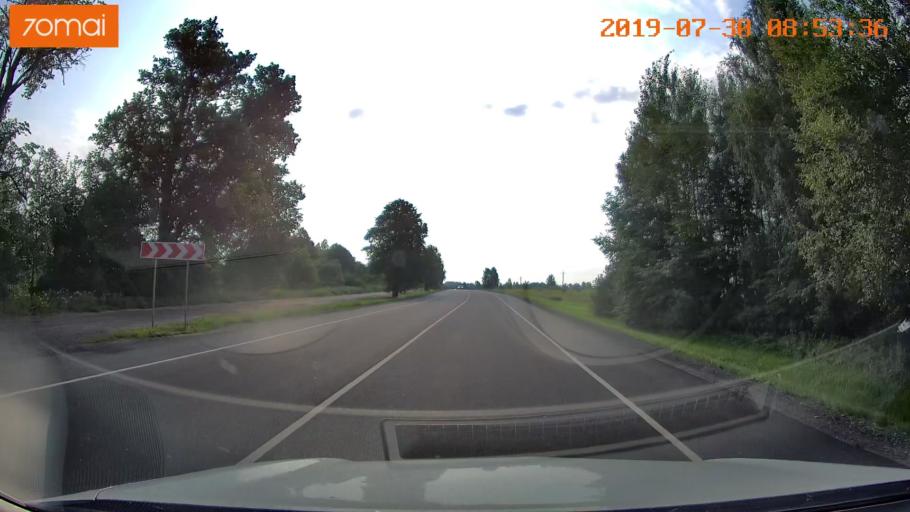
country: RU
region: Kaliningrad
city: Chernyakhovsk
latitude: 54.6012
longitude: 22.0025
